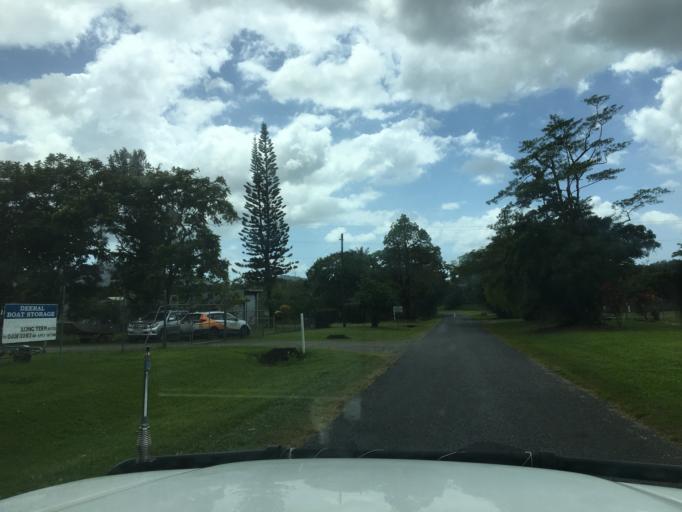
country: AU
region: Queensland
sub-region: Cairns
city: Woree
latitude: -17.2184
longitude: 145.9151
